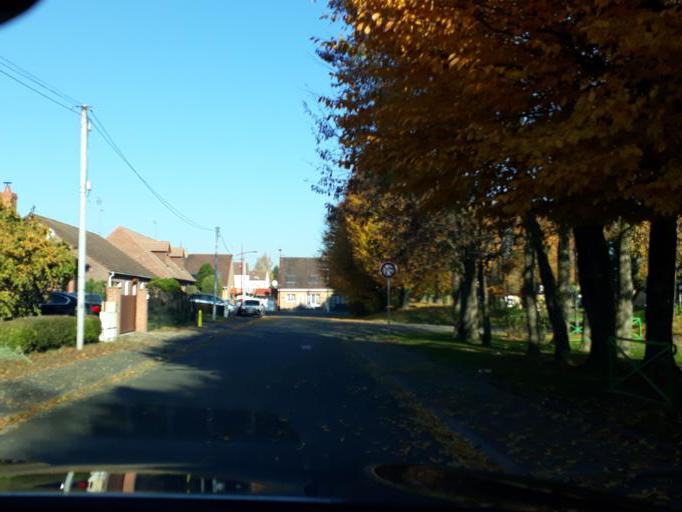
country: FR
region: Nord-Pas-de-Calais
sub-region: Departement du Nord
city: Masny
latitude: 50.3473
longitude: 3.2032
